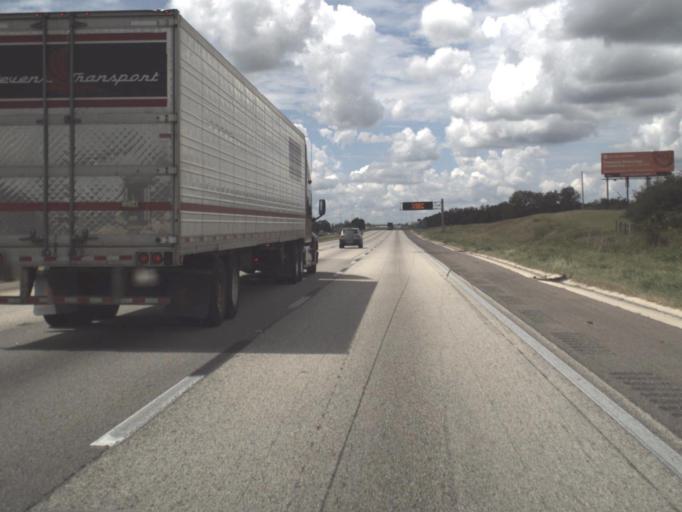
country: US
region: Florida
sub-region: Polk County
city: Loughman
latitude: 28.2488
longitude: -81.6284
